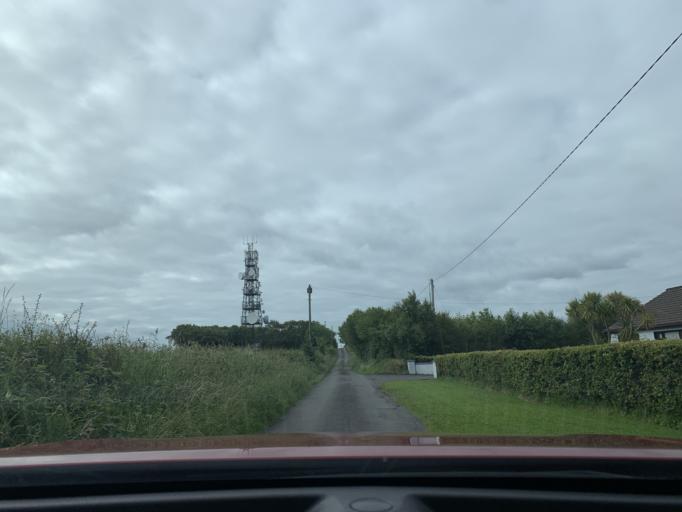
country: IE
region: Connaught
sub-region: Sligo
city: Sligo
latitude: 54.3703
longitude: -8.5204
